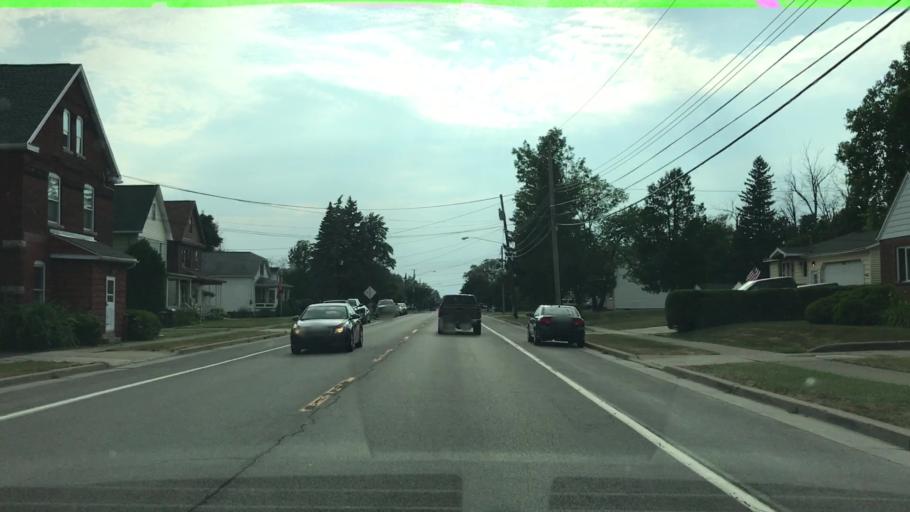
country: US
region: New York
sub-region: Erie County
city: Depew
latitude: 42.9147
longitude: -78.7000
